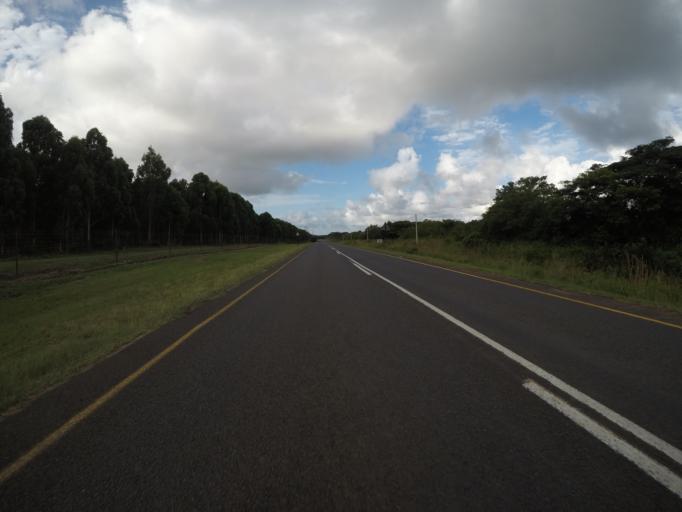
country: ZA
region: KwaZulu-Natal
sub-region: uMkhanyakude District Municipality
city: Mtubatuba
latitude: -28.3770
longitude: 32.2505
